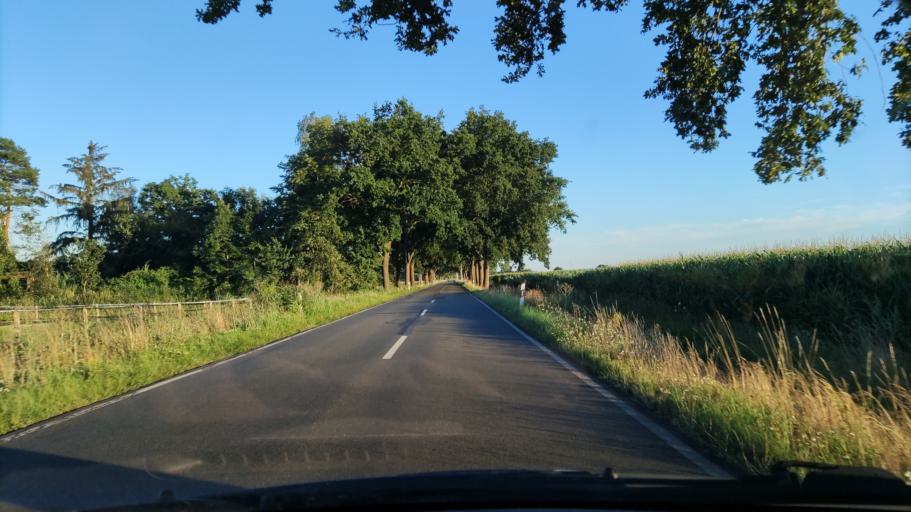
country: DE
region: Lower Saxony
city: Luechow
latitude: 52.9965
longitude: 11.1532
